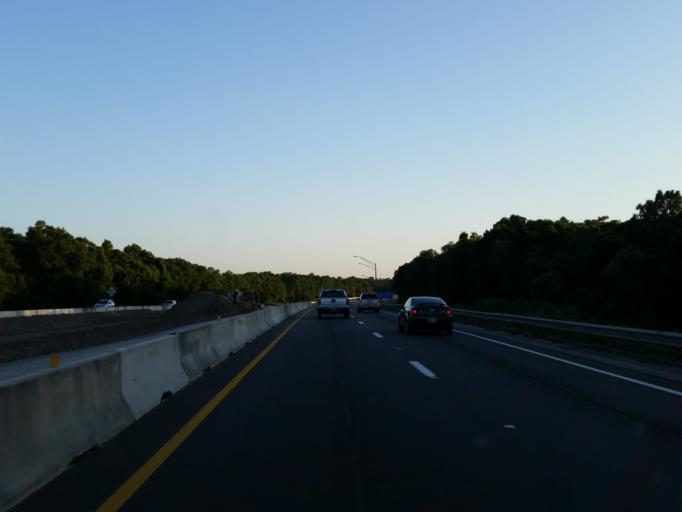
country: US
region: Florida
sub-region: Hernando County
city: Ridge Manor
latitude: 28.5918
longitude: -82.2081
